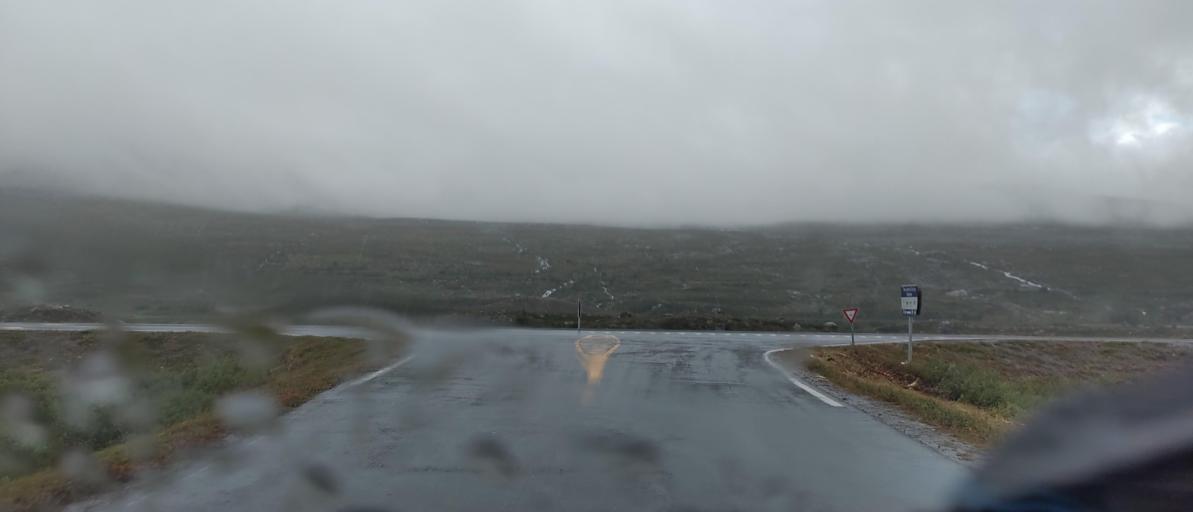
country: NO
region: Nordland
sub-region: Saltdal
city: Rognan
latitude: 66.5508
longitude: 15.3186
